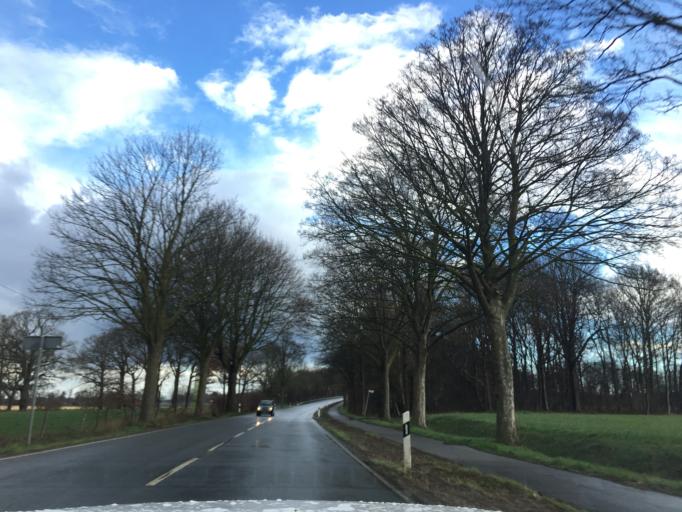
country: DE
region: North Rhine-Westphalia
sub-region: Regierungsbezirk Munster
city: Isselburg
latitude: 51.8007
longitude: 6.4772
